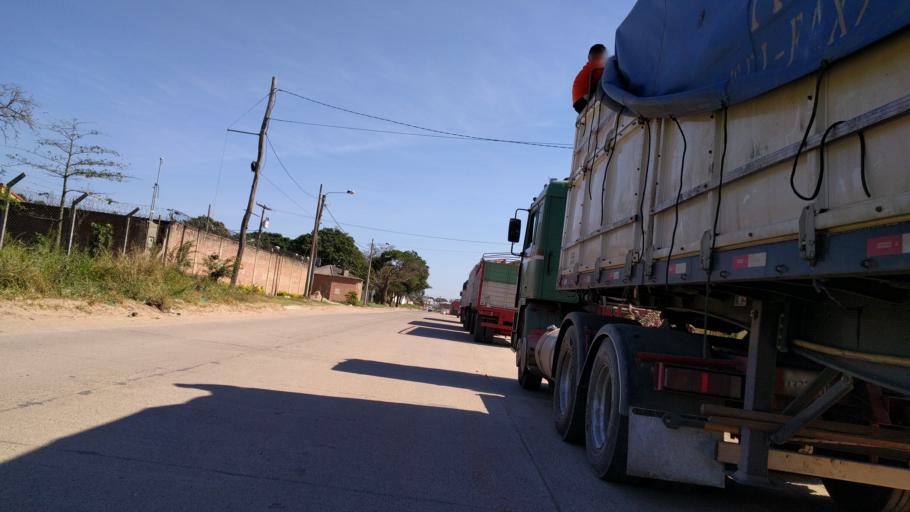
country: BO
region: Santa Cruz
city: Santa Cruz de la Sierra
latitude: -17.8402
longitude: -63.2348
